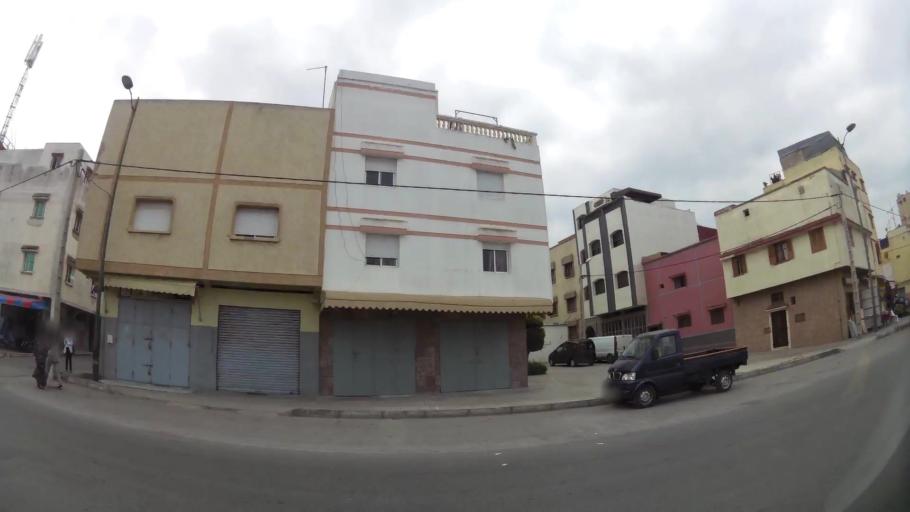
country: MA
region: Rabat-Sale-Zemmour-Zaer
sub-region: Rabat
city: Rabat
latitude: 34.0033
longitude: -6.8673
